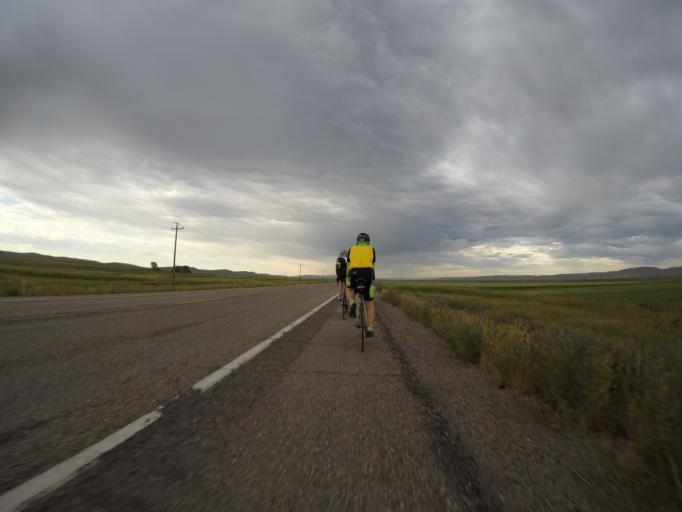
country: US
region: Utah
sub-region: Rich County
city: Randolph
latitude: 41.9515
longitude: -110.9502
